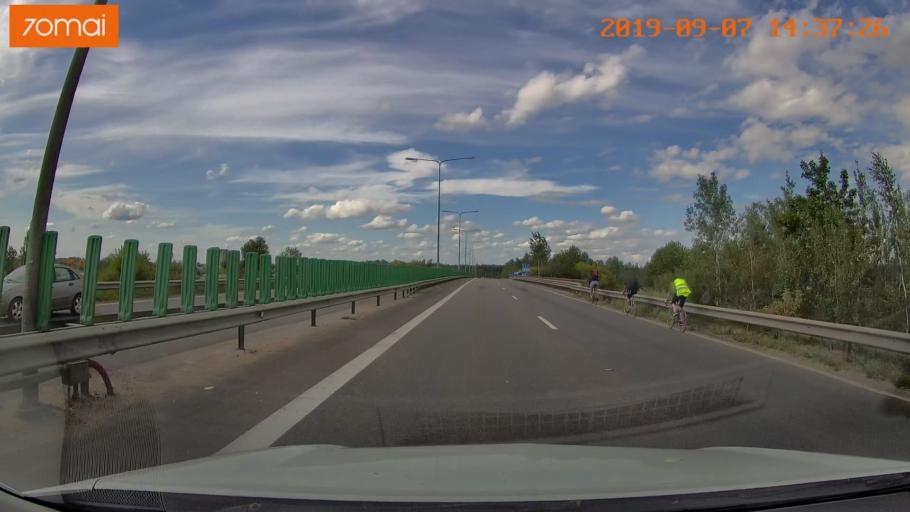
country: LT
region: Kauno apskritis
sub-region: Kauno rajonas
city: Karmelava
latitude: 54.9225
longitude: 24.0789
